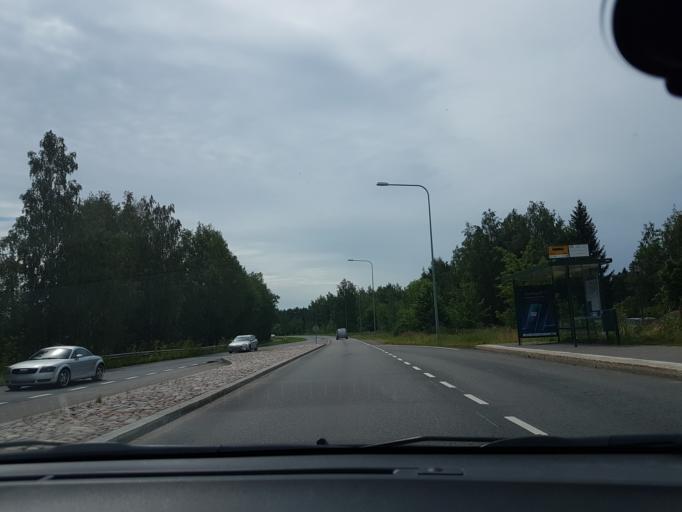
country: FI
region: Uusimaa
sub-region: Helsinki
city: Vantaa
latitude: 60.2622
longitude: 25.0402
